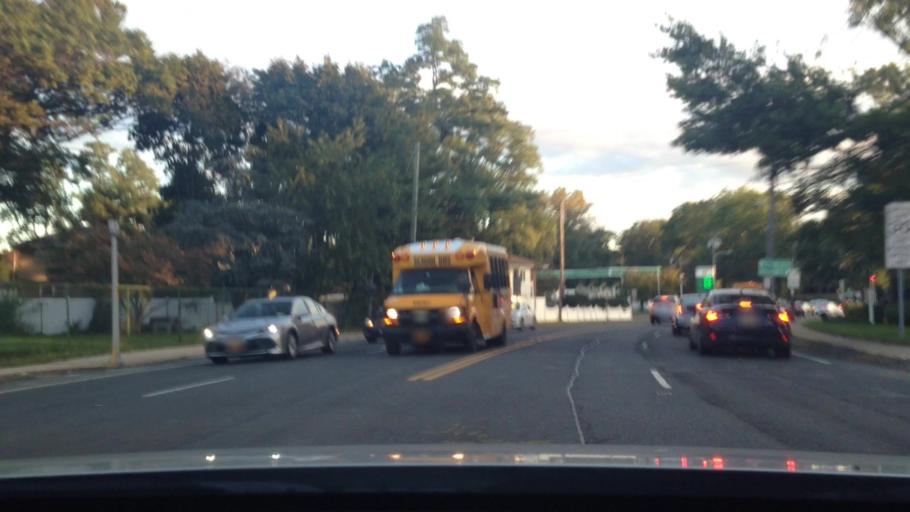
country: US
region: New York
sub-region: Nassau County
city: Lakeview
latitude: 40.6859
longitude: -73.6624
